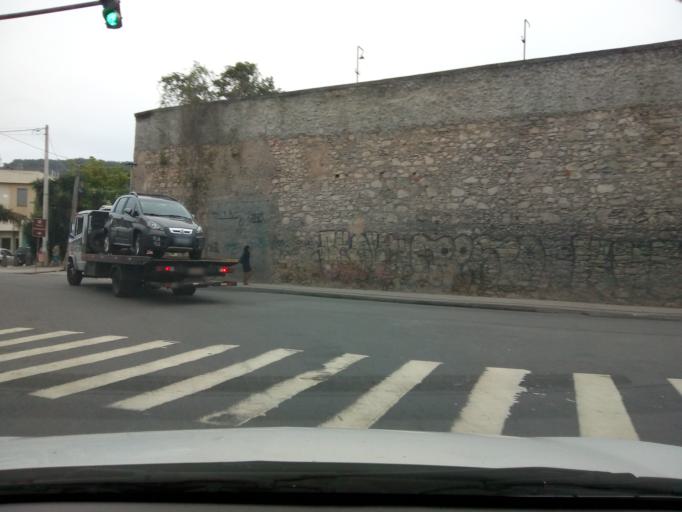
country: BR
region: Rio de Janeiro
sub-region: Rio De Janeiro
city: Rio de Janeiro
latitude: -22.9142
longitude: -43.1994
